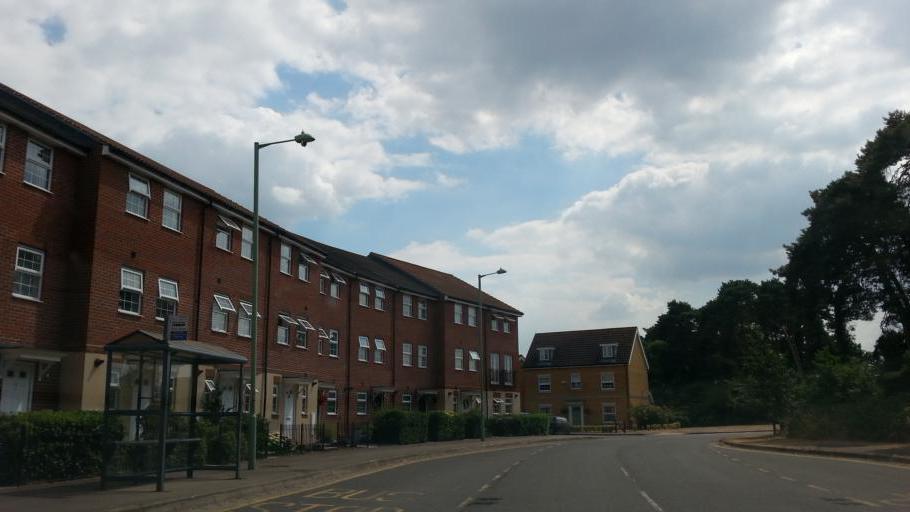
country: GB
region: England
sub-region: Cambridgeshire
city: Isleham
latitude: 52.3085
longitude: 0.4985
